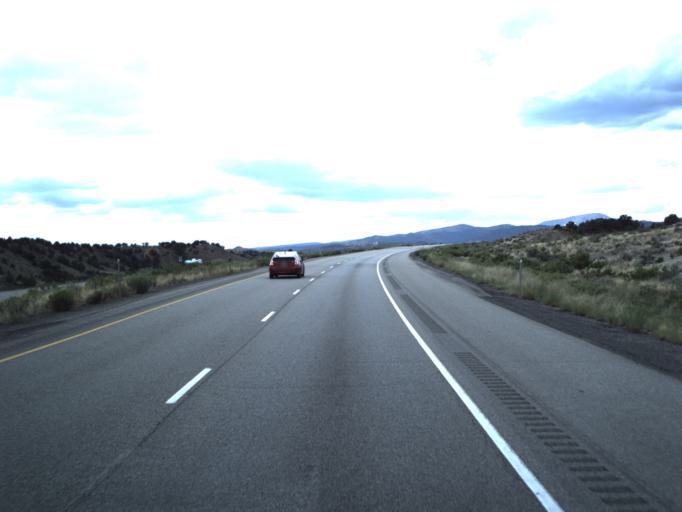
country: US
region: Utah
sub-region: Emery County
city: Ferron
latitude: 38.7840
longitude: -111.3045
